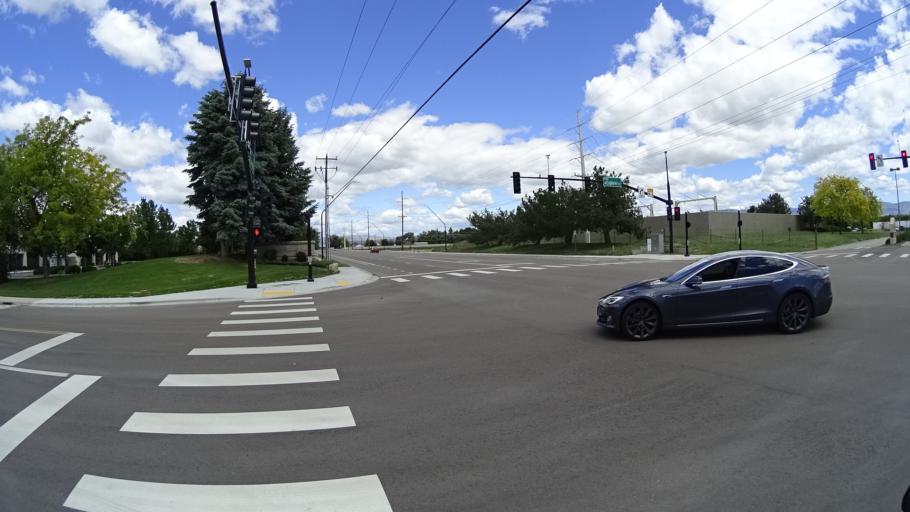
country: US
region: Idaho
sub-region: Ada County
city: Eagle
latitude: 43.6594
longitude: -116.3347
